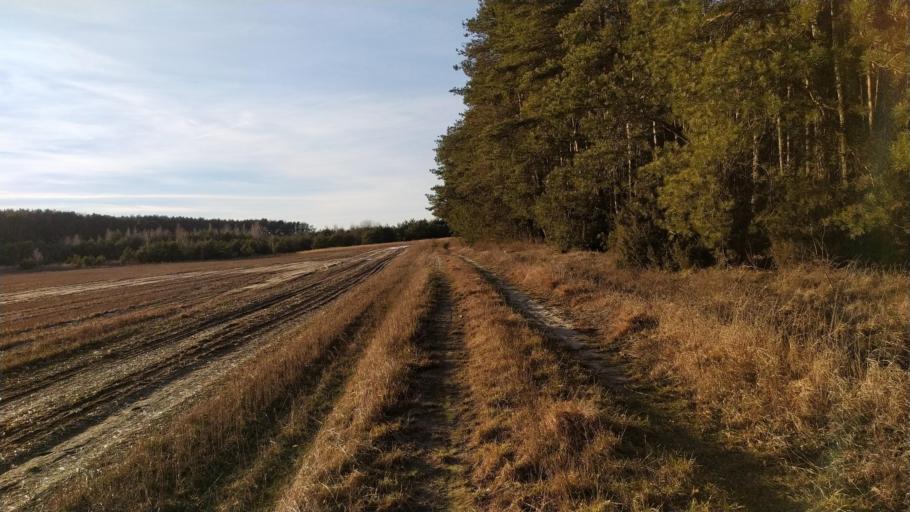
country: BY
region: Brest
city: Kamyanyets
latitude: 52.3711
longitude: 23.8503
